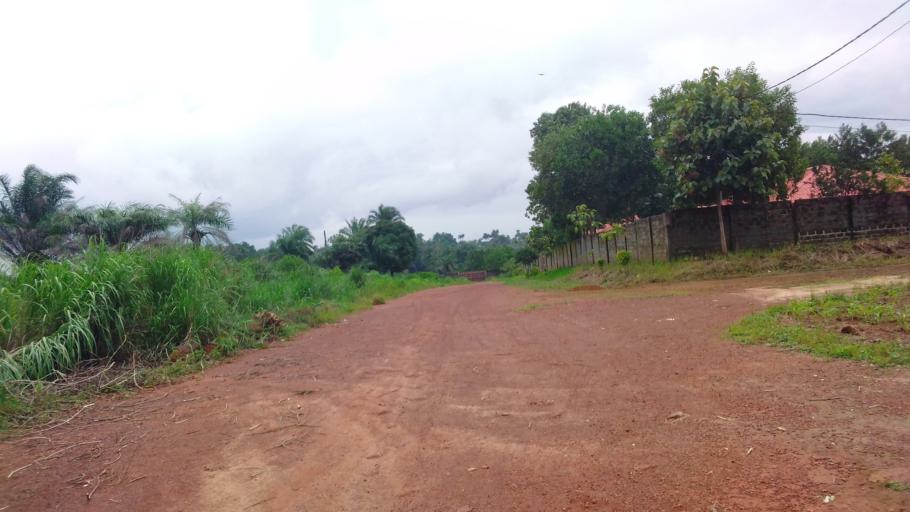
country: SL
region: Northern Province
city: Lunsar
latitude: 8.6942
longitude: -12.5496
